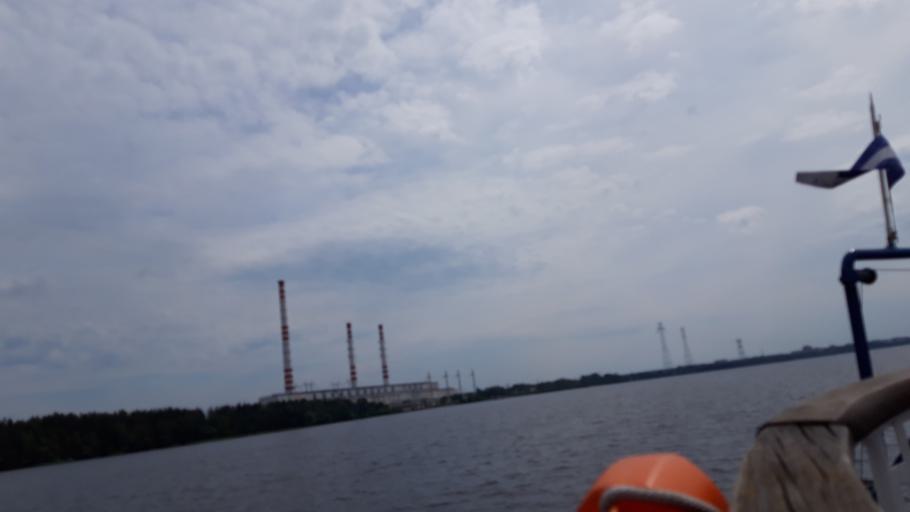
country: RU
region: Tverskaya
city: Konakovo
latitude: 56.7479
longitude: 36.7540
